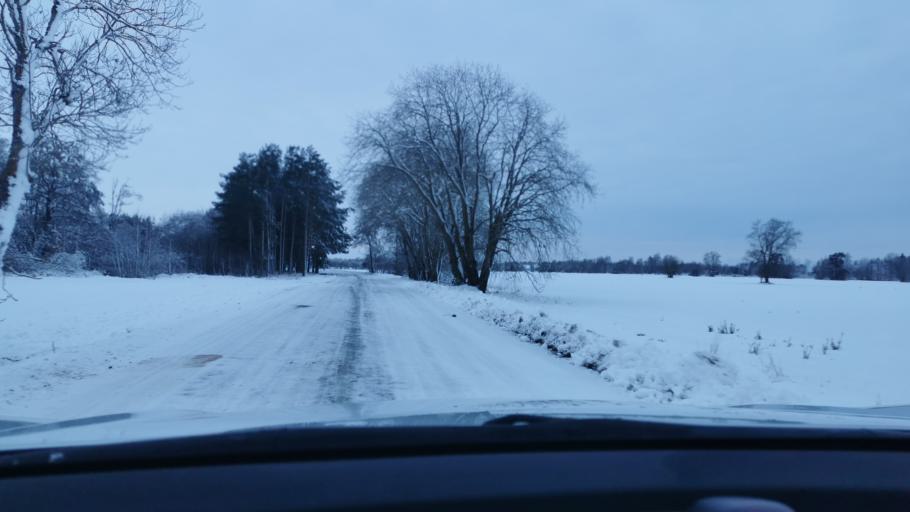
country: EE
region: Laeaene-Virumaa
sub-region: Viru-Nigula vald
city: Kunda
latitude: 59.4528
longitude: 26.5196
